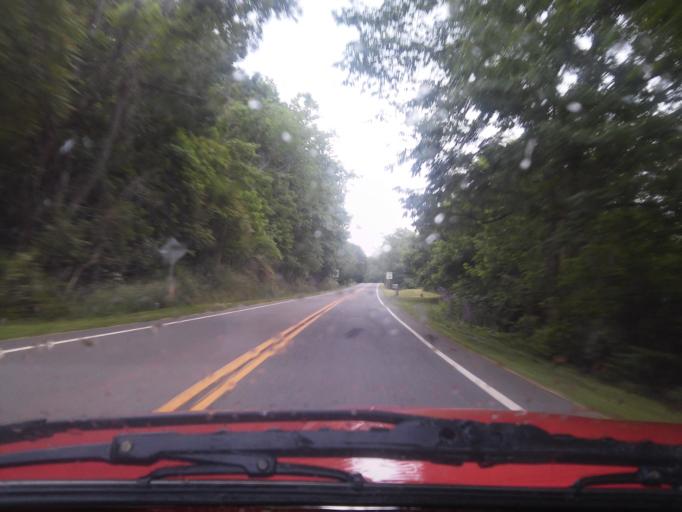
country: US
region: Virginia
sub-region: Montgomery County
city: Prices Fork
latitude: 37.3059
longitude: -80.4816
